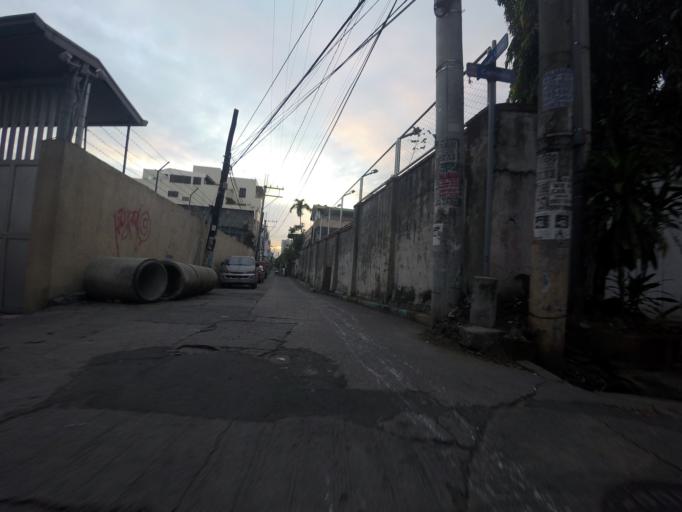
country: PH
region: Metro Manila
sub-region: San Juan
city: San Juan
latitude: 14.6004
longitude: 121.0309
